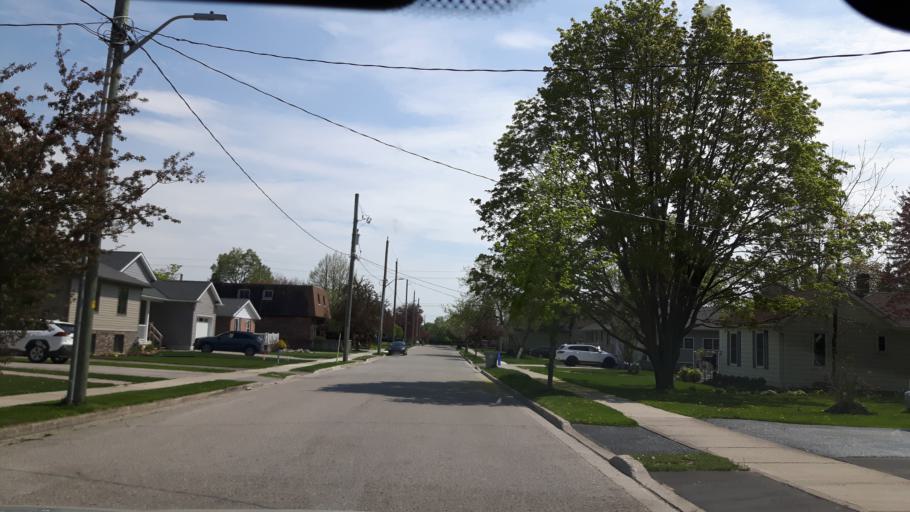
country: CA
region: Ontario
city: Goderich
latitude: 43.7385
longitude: -81.7179
